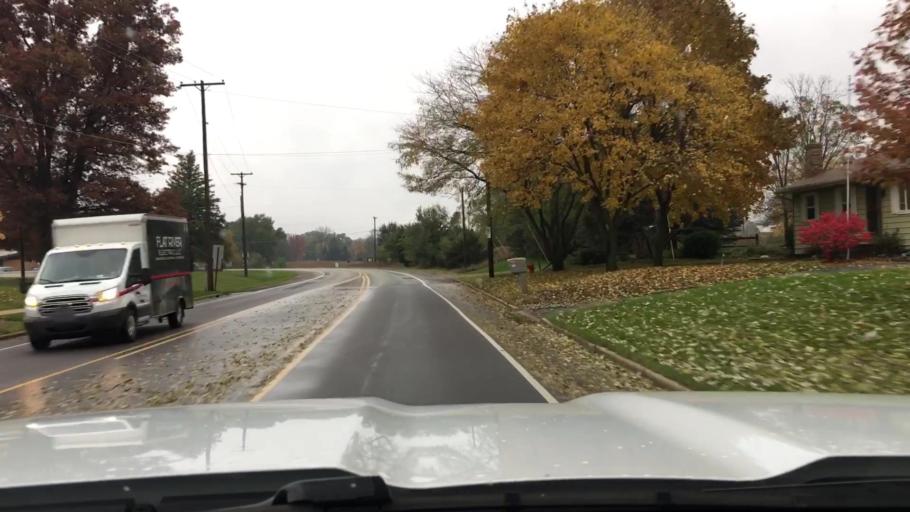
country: US
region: Michigan
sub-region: Kent County
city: Lowell
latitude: 42.9436
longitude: -85.3454
